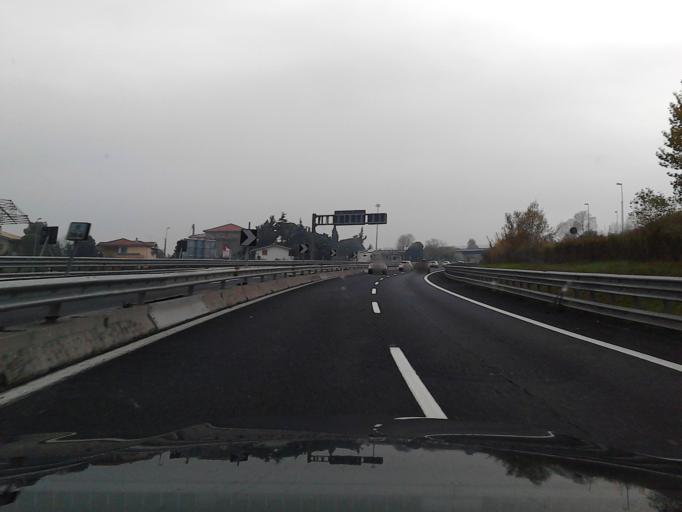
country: IT
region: Abruzzo
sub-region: Provincia di Pescara
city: San Martino Bassa
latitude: 42.5185
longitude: 14.1332
